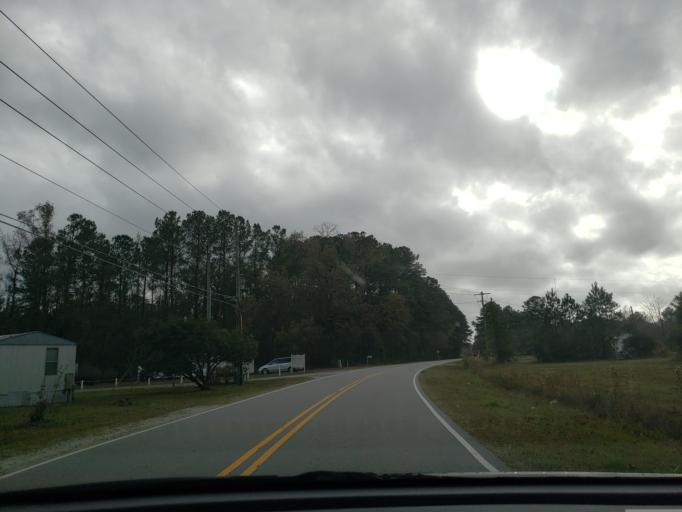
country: US
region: North Carolina
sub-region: Onslow County
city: Jacksonville
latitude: 34.7136
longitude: -77.5782
